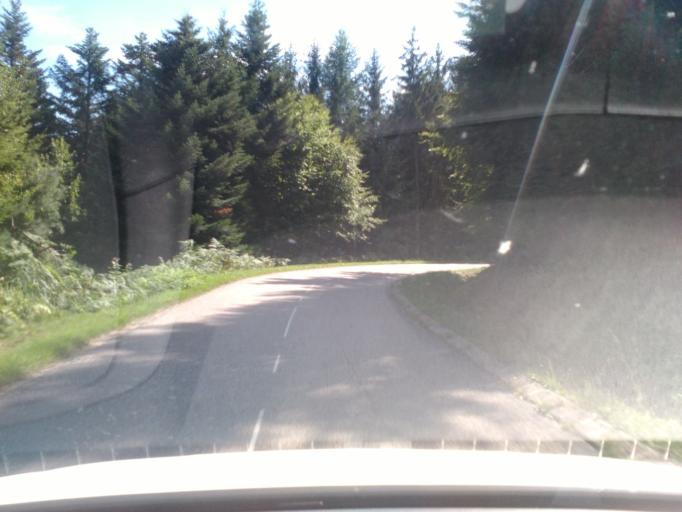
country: FR
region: Lorraine
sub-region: Departement des Vosges
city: Senones
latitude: 48.3688
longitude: 6.9735
